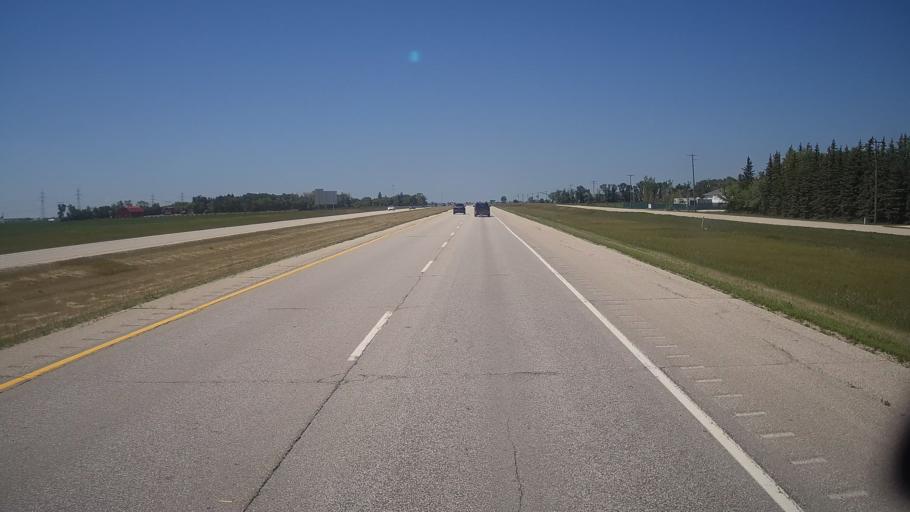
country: CA
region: Manitoba
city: Winnipeg
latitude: 49.9900
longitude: -97.2629
